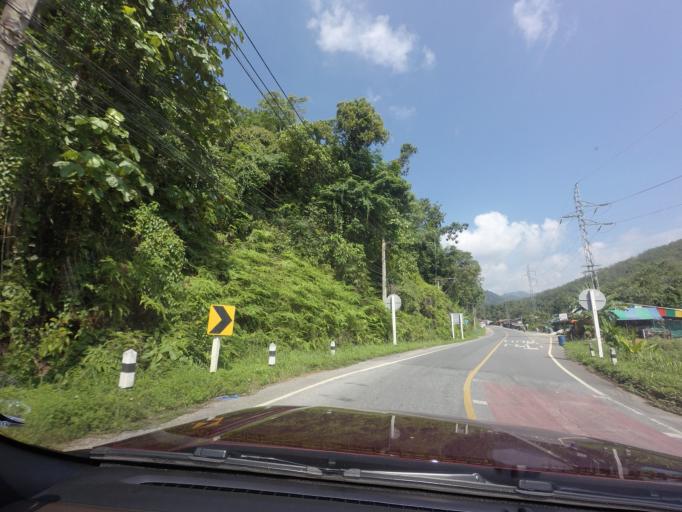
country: TH
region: Yala
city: Betong
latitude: 5.9171
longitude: 101.1752
